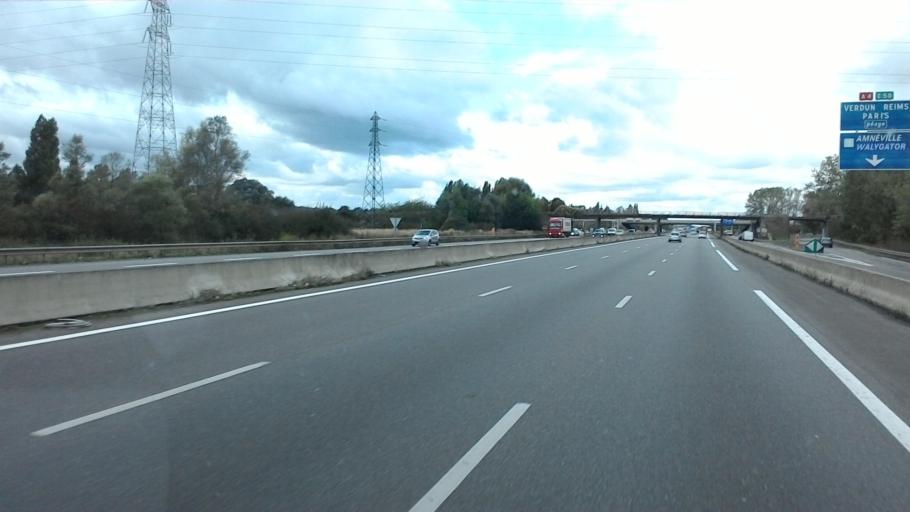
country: FR
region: Lorraine
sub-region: Departement de la Moselle
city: Maizieres-les-Metz
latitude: 49.1966
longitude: 6.1756
